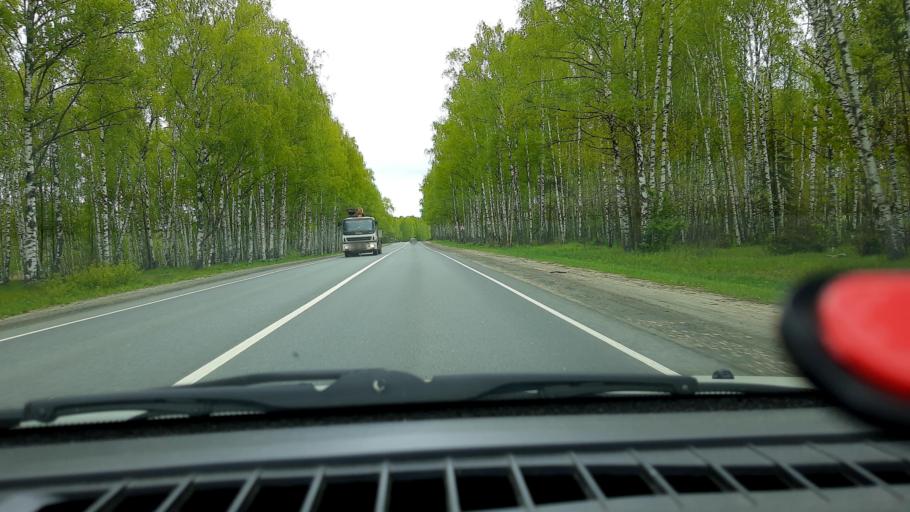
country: RU
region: Nizjnij Novgorod
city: Linda
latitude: 56.6721
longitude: 44.1423
